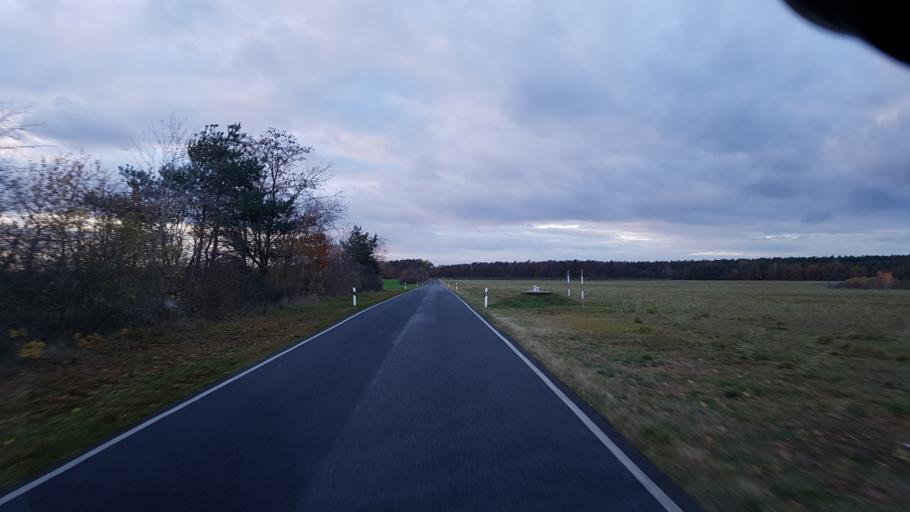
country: DE
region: Brandenburg
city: Tettau
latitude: 51.4215
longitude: 13.7515
